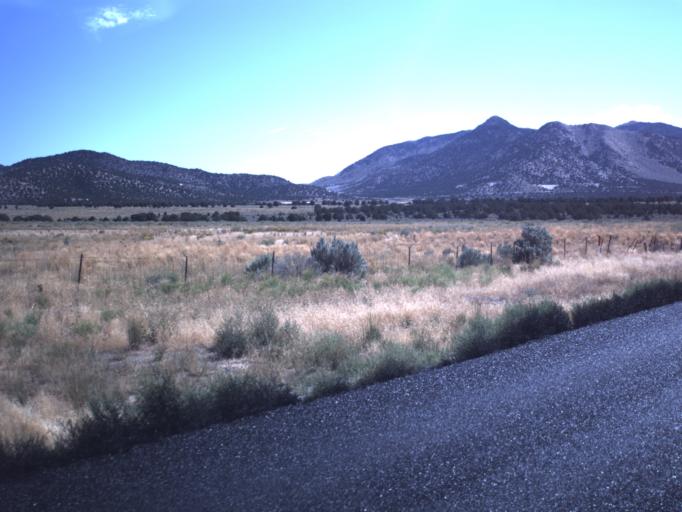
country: US
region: Utah
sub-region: Utah County
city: Genola
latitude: 39.9393
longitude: -112.1842
